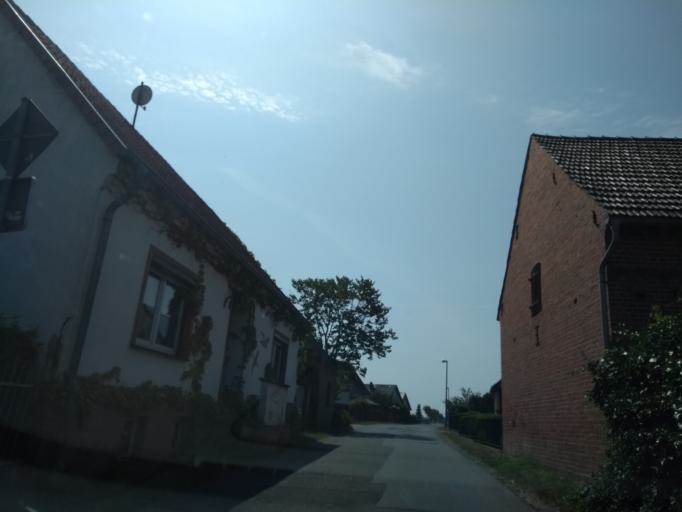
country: DE
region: Brandenburg
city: Vetschau
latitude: 51.8169
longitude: 14.0443
